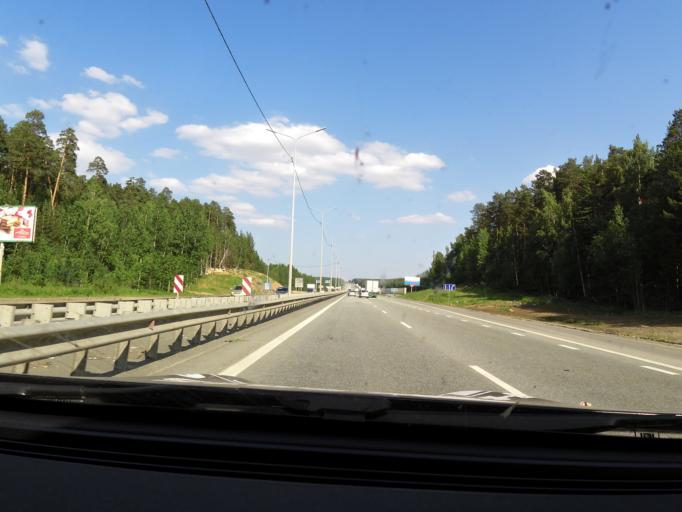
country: RU
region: Sverdlovsk
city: Shirokaya Rechka
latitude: 56.8302
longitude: 60.4026
